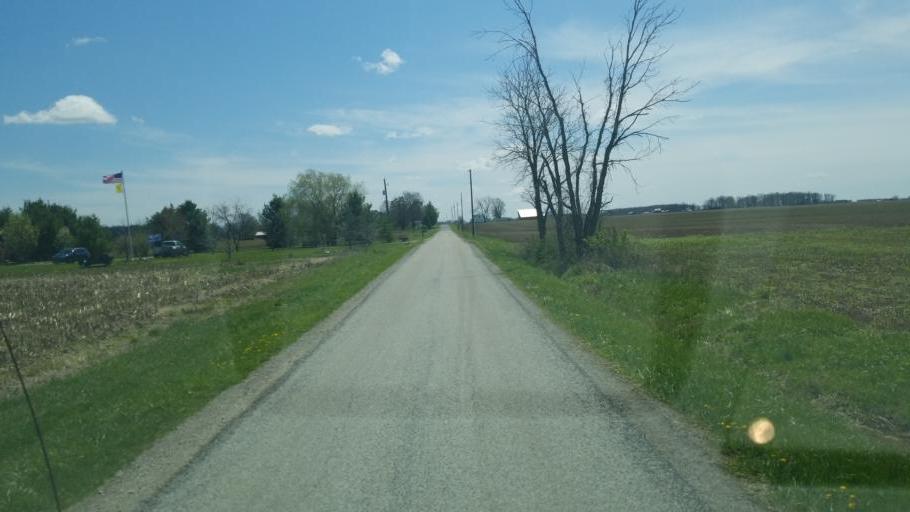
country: US
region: Ohio
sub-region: Union County
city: Richwood
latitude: 40.5086
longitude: -83.2906
